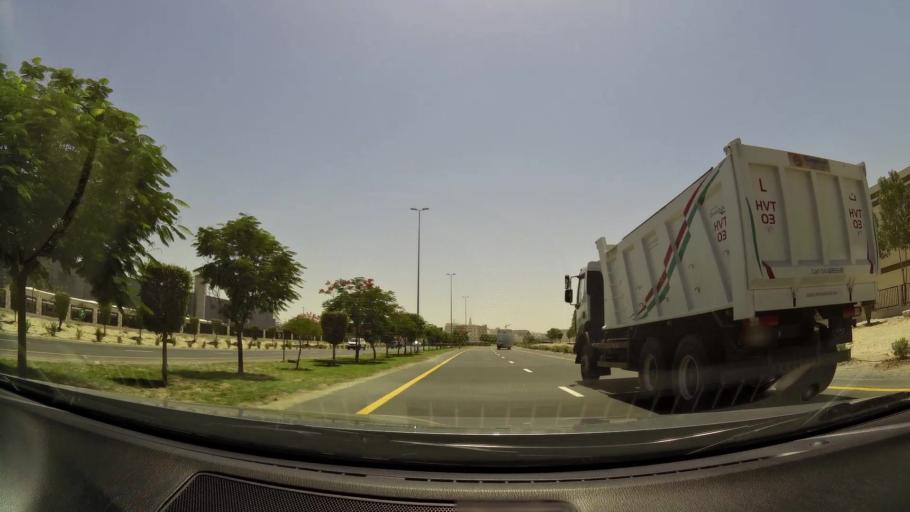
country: AE
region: Dubai
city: Dubai
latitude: 24.9735
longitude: 55.1953
